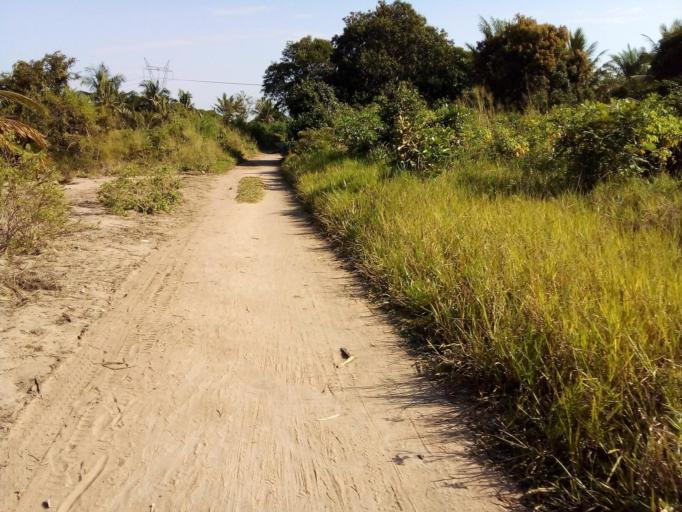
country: MZ
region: Zambezia
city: Quelimane
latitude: -17.5219
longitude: 36.8449
